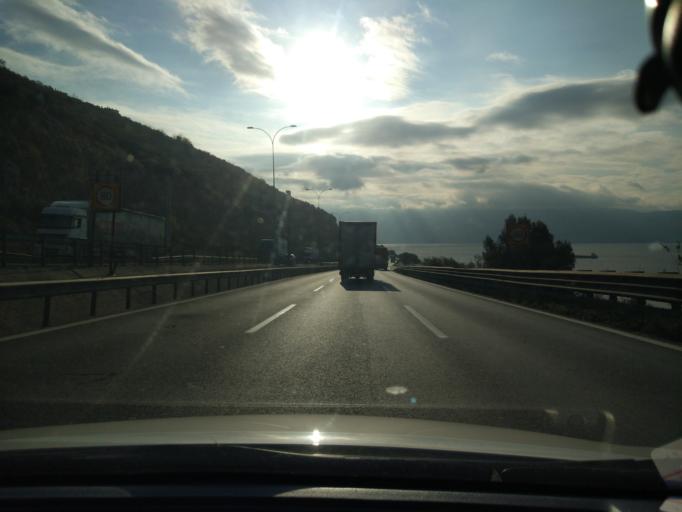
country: TR
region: Kocaeli
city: Hereke
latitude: 40.7829
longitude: 29.6266
